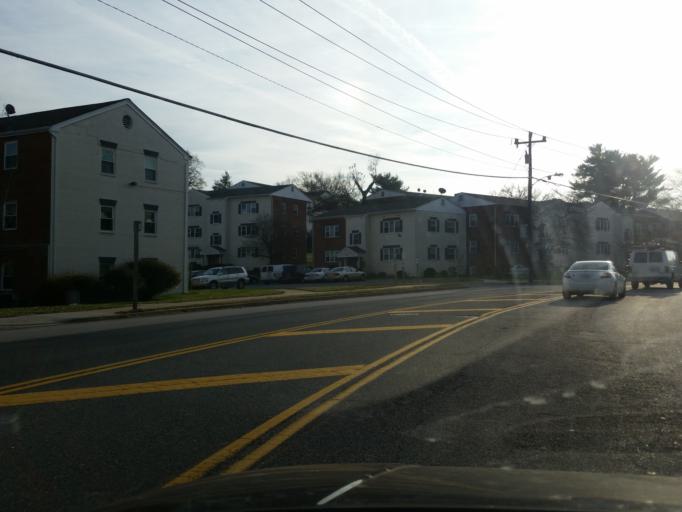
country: US
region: Virginia
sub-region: Fairfax County
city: Seven Corners
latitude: 38.8670
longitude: -77.1479
